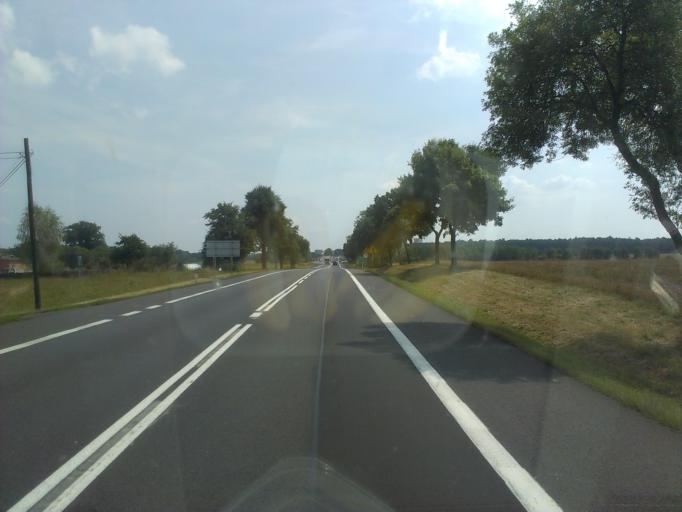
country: PL
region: Lower Silesian Voivodeship
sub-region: Powiat polkowicki
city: Radwanice
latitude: 51.5660
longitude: 16.0207
